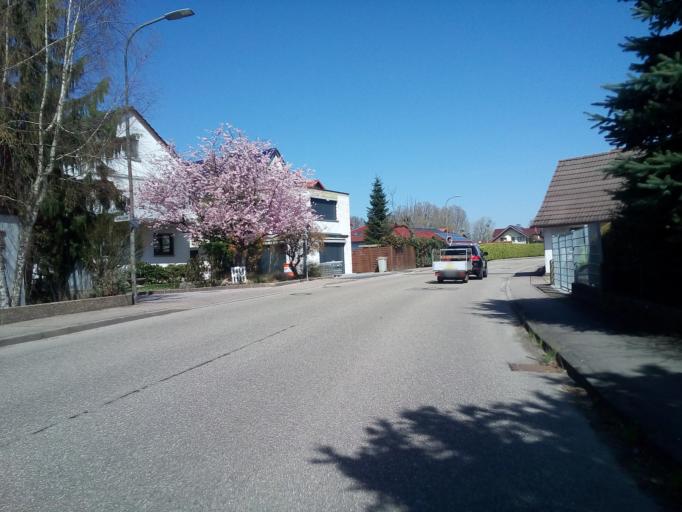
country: FR
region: Alsace
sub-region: Departement du Bas-Rhin
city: Kilstett
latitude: 48.6414
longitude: 7.8725
